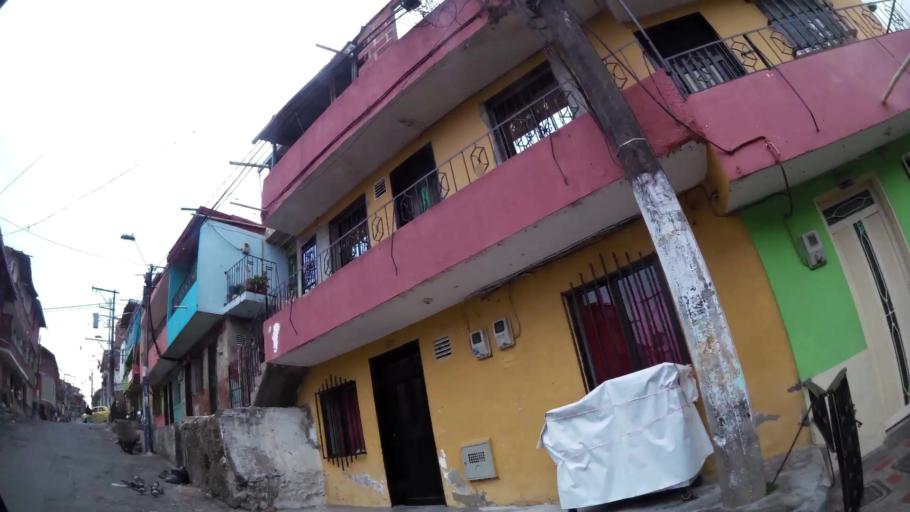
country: CO
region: Antioquia
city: Medellin
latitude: 6.2856
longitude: -75.5453
